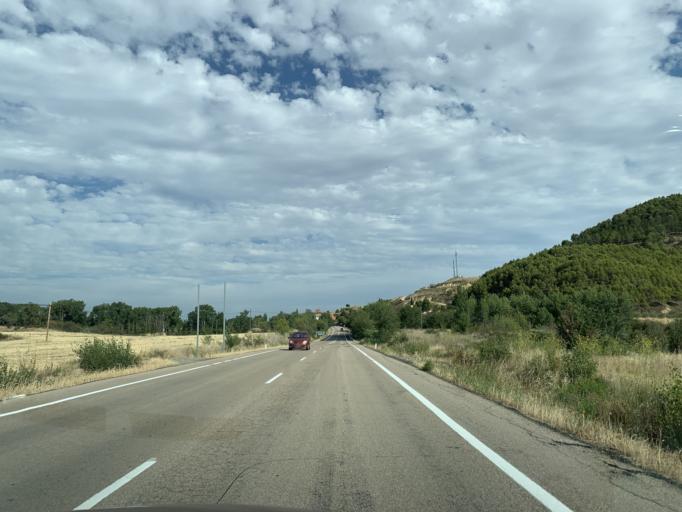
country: ES
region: Aragon
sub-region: Provincia de Huesca
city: Ayerbe
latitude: 42.2813
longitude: -0.6976
